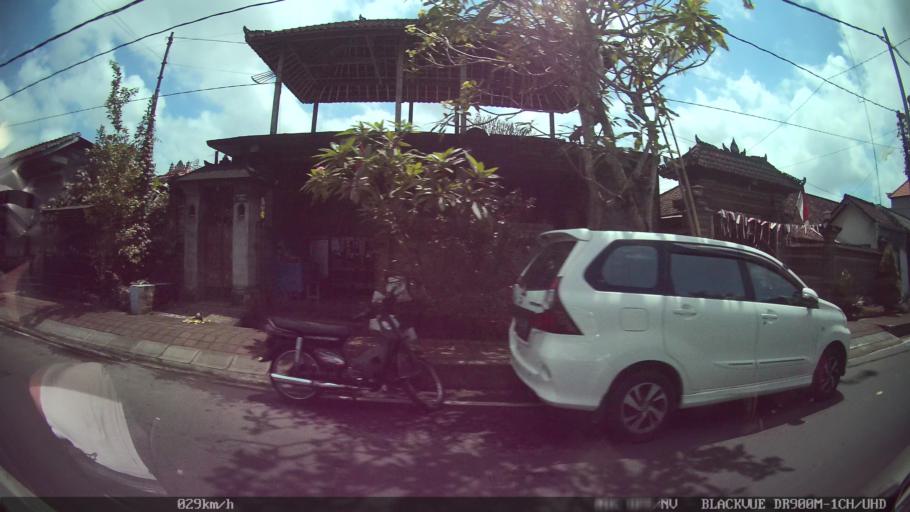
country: ID
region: Bali
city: Banjar Pasekan
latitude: -8.5923
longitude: 115.2838
